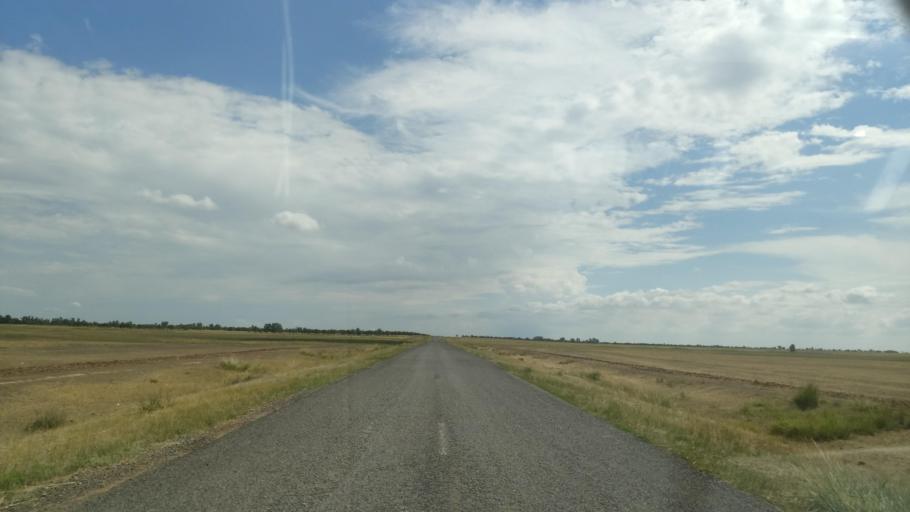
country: KZ
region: Pavlodar
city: Pavlodar
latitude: 52.6361
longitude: 76.9486
